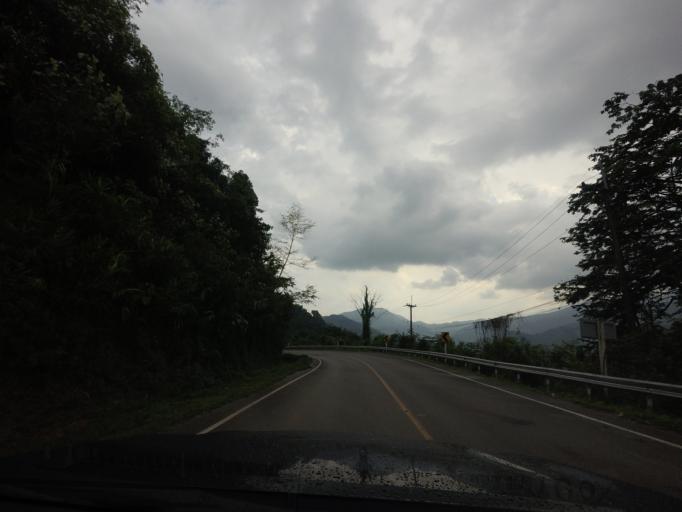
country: TH
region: Nan
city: Bo Kluea
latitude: 19.1677
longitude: 101.1430
